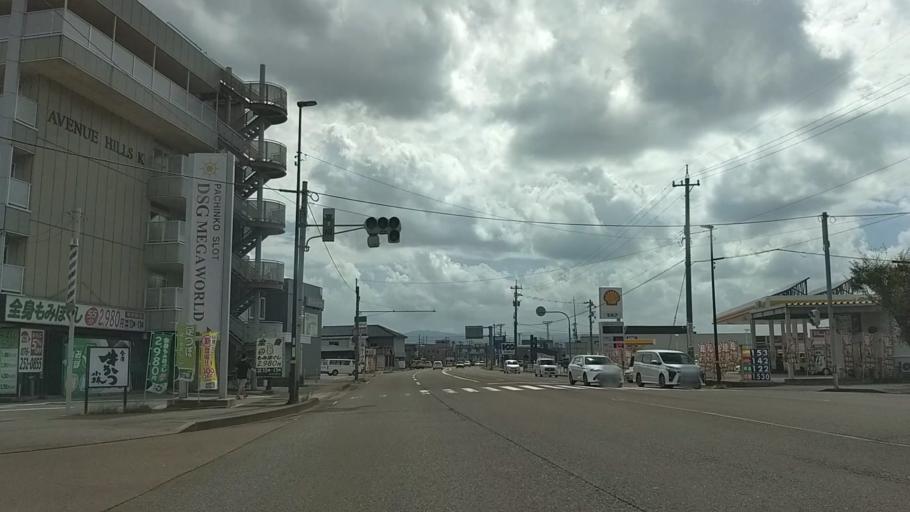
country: JP
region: Ishikawa
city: Kanazawa-shi
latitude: 36.5947
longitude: 136.6630
